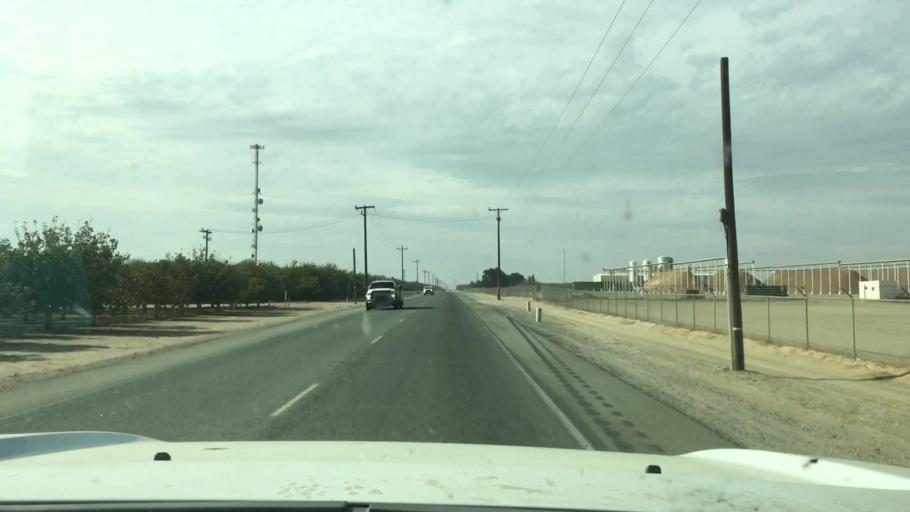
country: US
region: California
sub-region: Kern County
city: Buttonwillow
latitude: 35.5006
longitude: -119.5004
